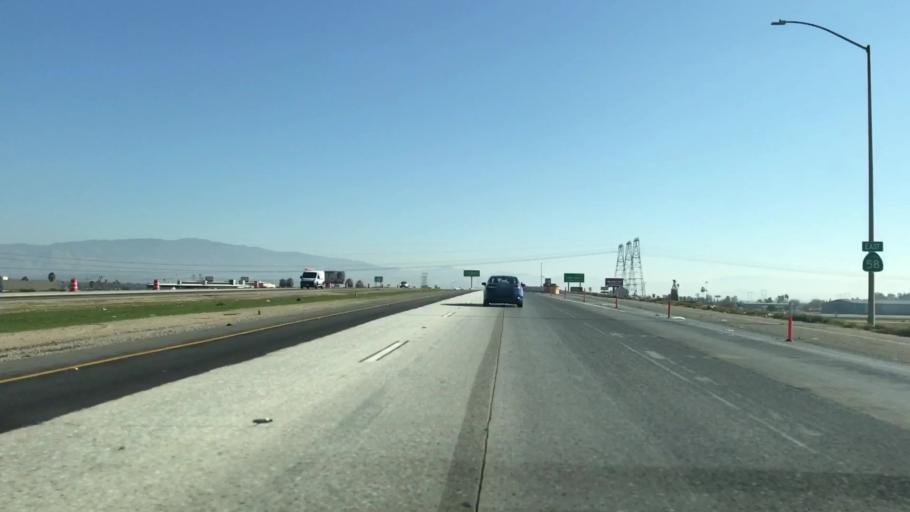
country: US
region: California
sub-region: Kern County
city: Lamont
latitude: 35.3516
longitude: -118.9275
